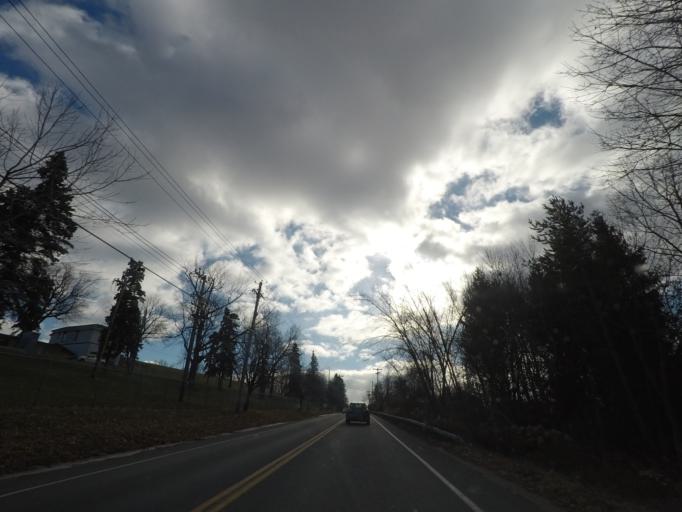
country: US
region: New York
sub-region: Schenectady County
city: Schenectady
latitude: 42.8086
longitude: -73.8929
